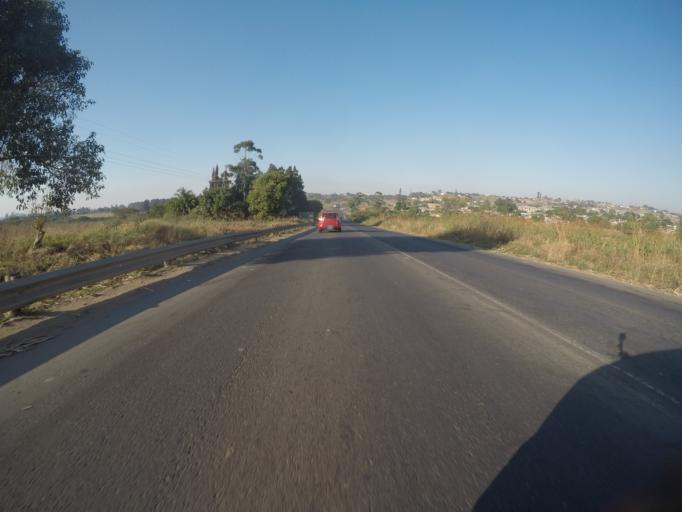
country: ZA
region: KwaZulu-Natal
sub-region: iLembe District Municipality
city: Stanger
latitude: -29.3950
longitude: 31.2516
